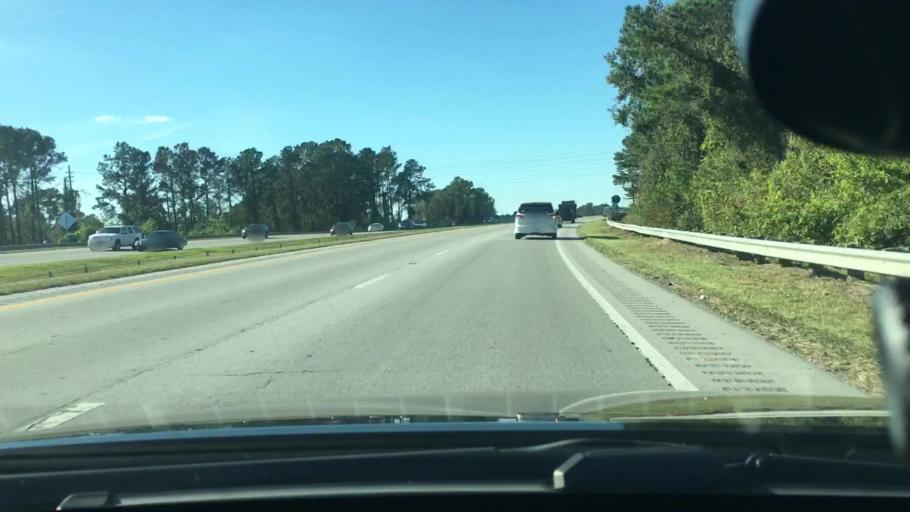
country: US
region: North Carolina
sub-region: Craven County
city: Trent Woods
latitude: 35.1007
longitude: -77.0789
